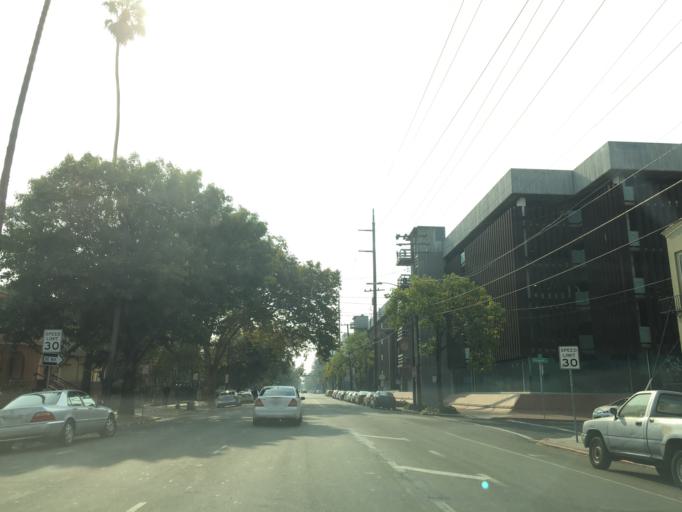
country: US
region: California
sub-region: Santa Clara County
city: San Jose
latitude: 37.3404
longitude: -121.8808
